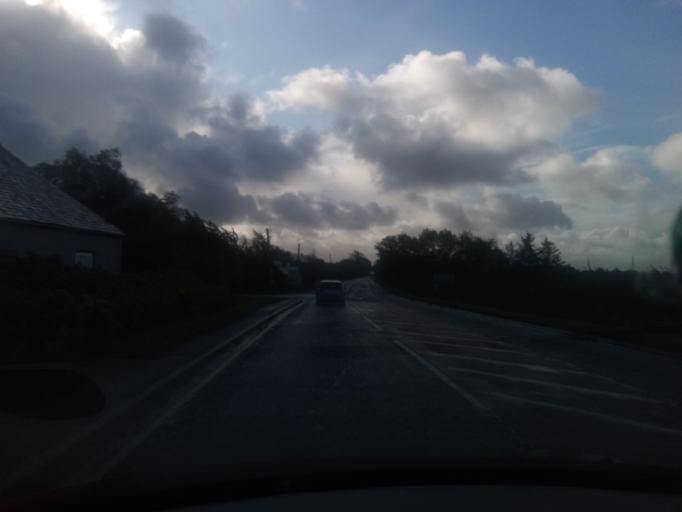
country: GB
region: England
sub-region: Cumbria
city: Carlisle
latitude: 54.9512
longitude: -2.9433
